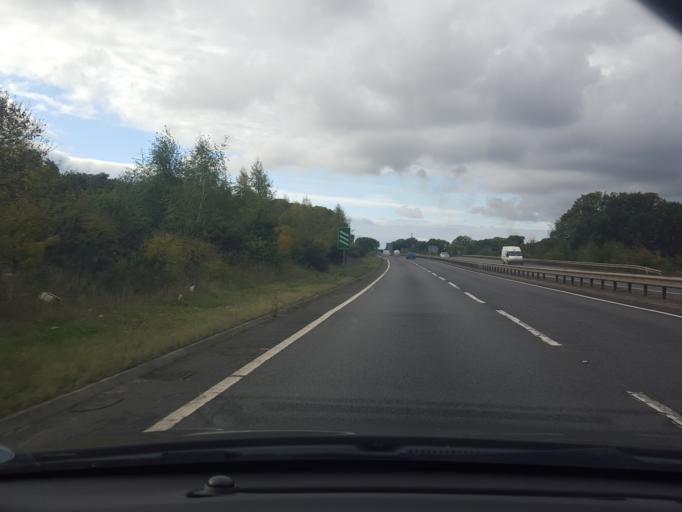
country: GB
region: England
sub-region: Suffolk
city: Thurston
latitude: 52.2378
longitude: 0.7862
